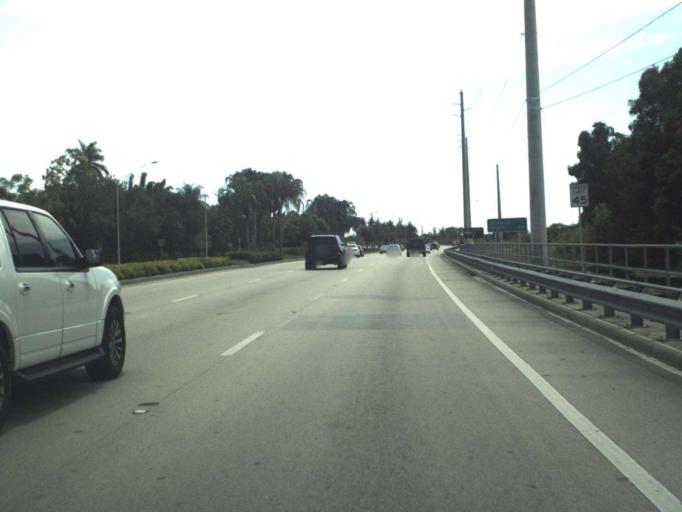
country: US
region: Florida
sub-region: Indian River County
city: Florida Ridge
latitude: 27.6081
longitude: -80.3836
